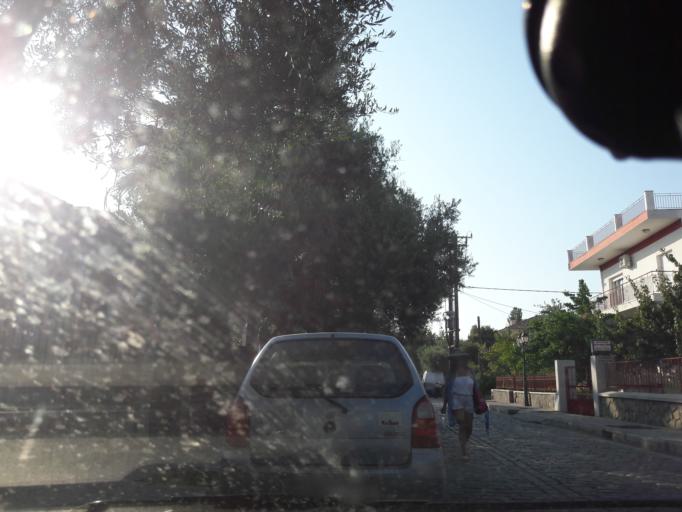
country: GR
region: North Aegean
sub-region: Nomos Lesvou
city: Myrina
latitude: 39.8755
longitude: 25.0632
